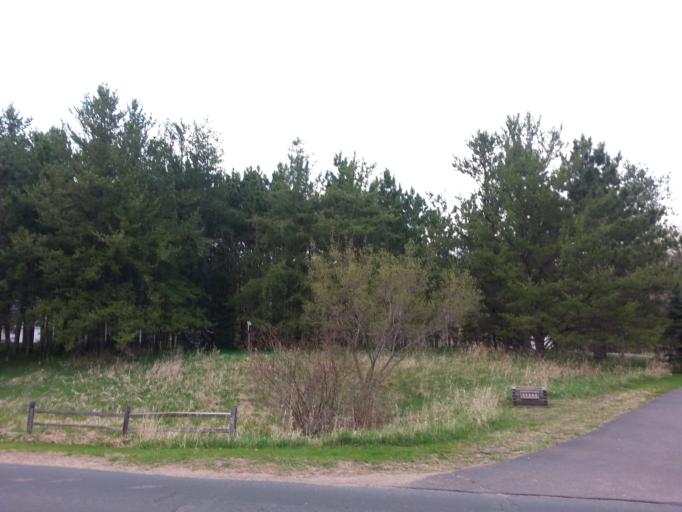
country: US
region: Minnesota
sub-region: Washington County
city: Lake Elmo
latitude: 44.9649
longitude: -92.8455
